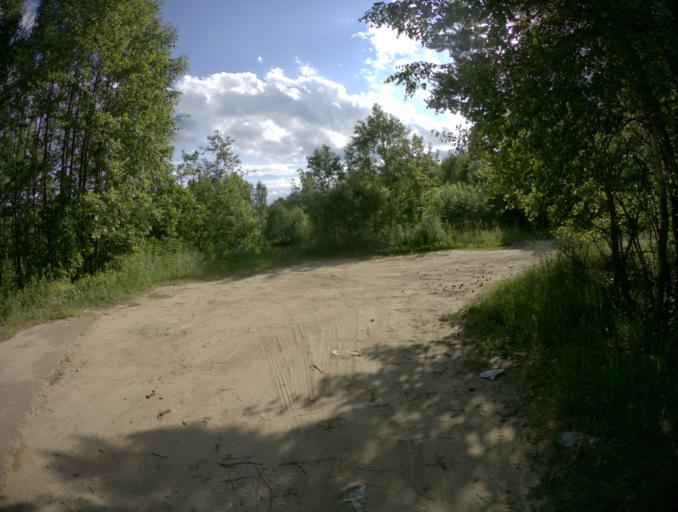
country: RU
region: Vladimir
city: Galitsy
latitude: 56.2464
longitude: 42.8361
